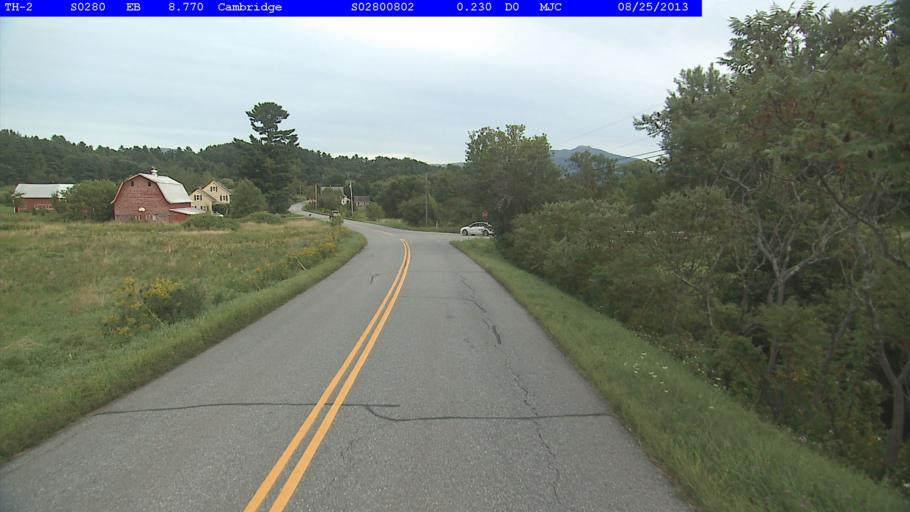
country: US
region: Vermont
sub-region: Chittenden County
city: Jericho
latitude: 44.6589
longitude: -72.8848
